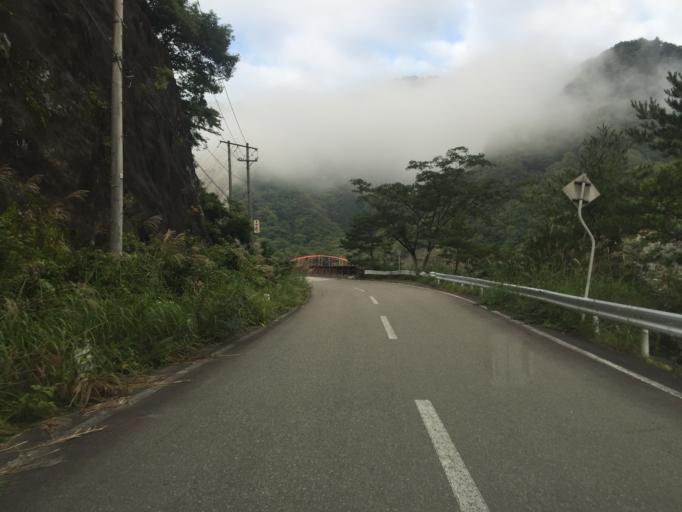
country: JP
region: Fukushima
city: Inawashiro
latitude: 37.4596
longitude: 139.9678
